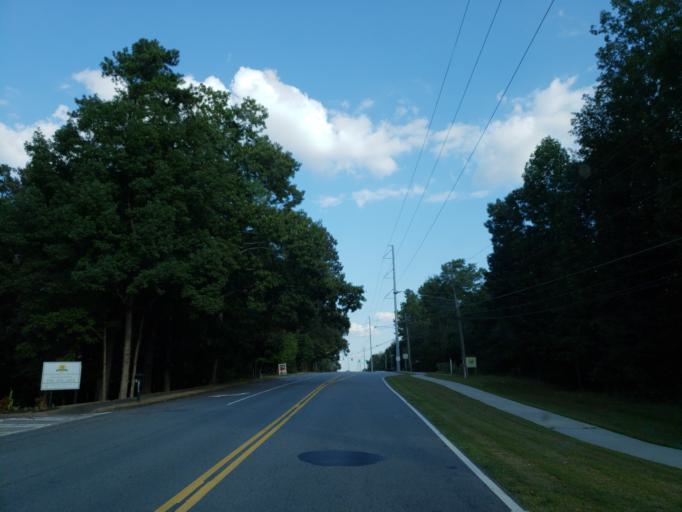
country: US
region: Georgia
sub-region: Fulton County
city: Alpharetta
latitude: 34.0686
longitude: -84.3281
